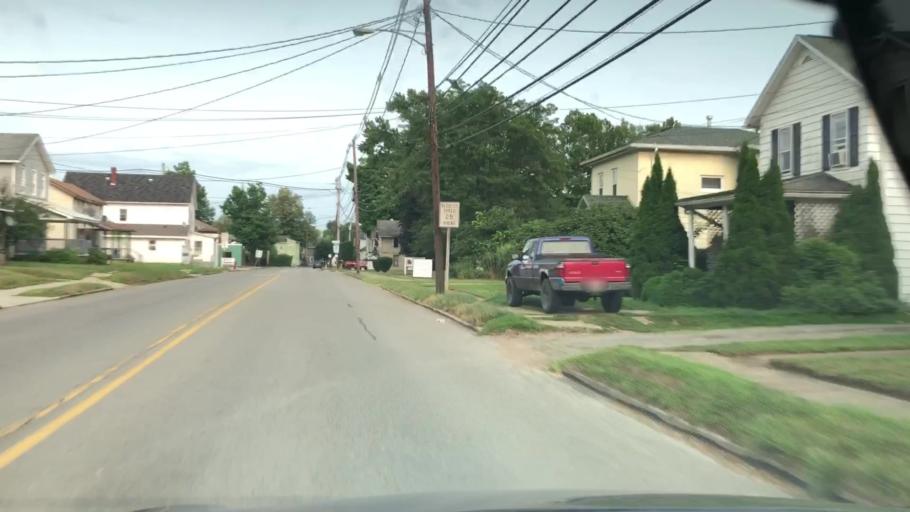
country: US
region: Pennsylvania
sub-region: Crawford County
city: Titusville
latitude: 41.6319
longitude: -79.6897
